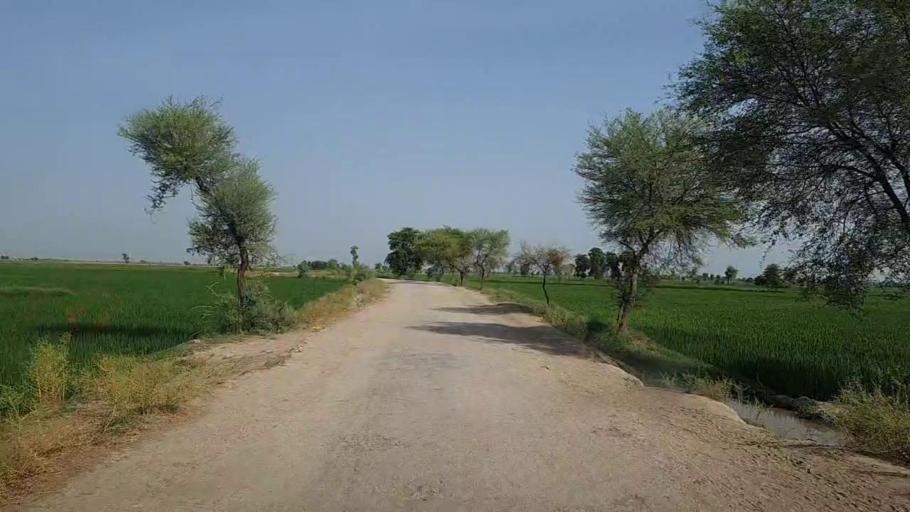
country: PK
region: Sindh
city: Sita Road
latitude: 27.1087
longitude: 67.8478
